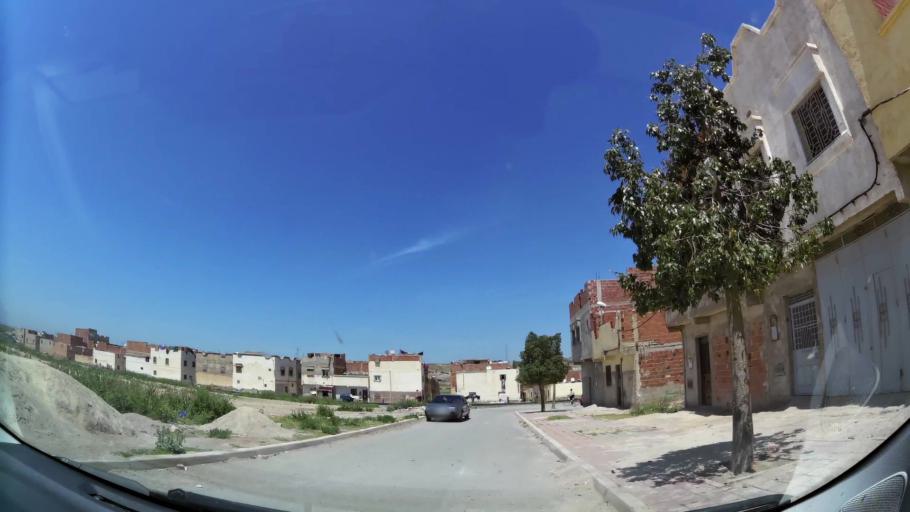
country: MA
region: Oriental
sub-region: Oujda-Angad
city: Oujda
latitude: 34.6950
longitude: -1.9480
